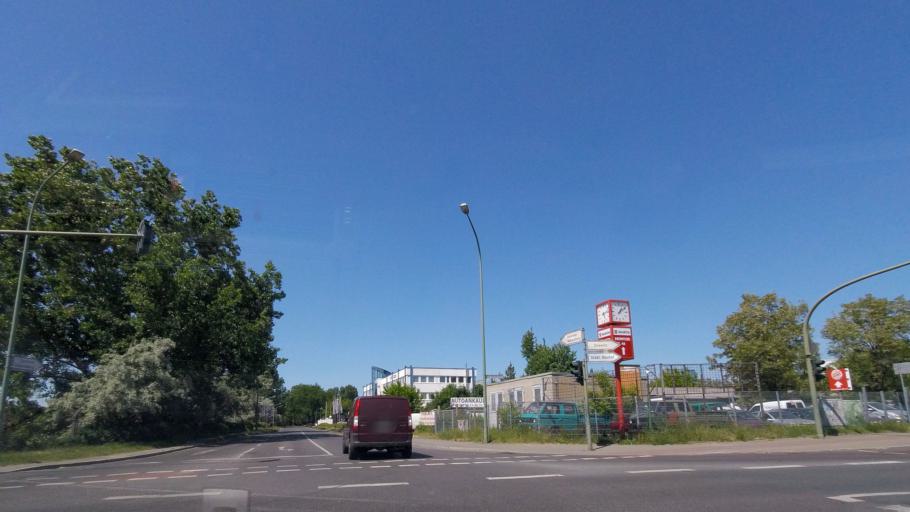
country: DE
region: Brandenburg
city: Potsdam
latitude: 52.3602
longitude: 13.1124
